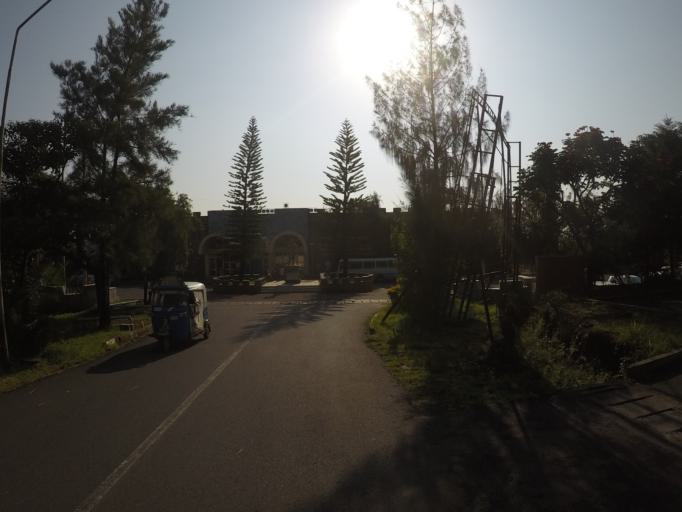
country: ET
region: Amhara
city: Gondar
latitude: 12.5165
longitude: 37.4293
